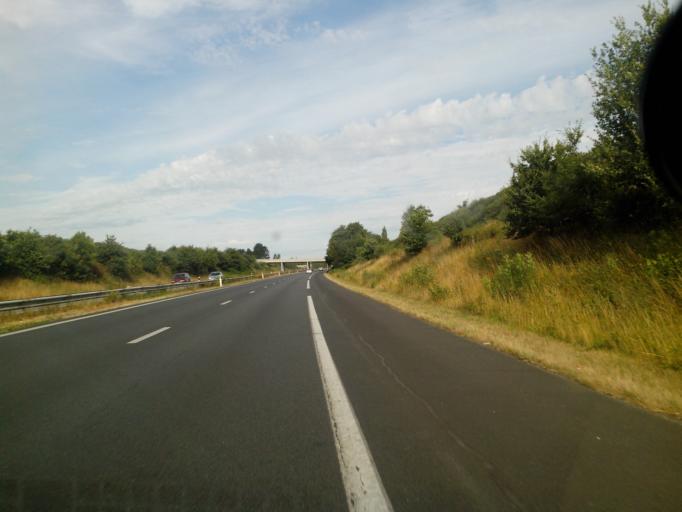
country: FR
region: Pays de la Loire
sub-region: Departement de la Loire-Atlantique
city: Sautron
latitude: 47.2543
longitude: -1.6764
